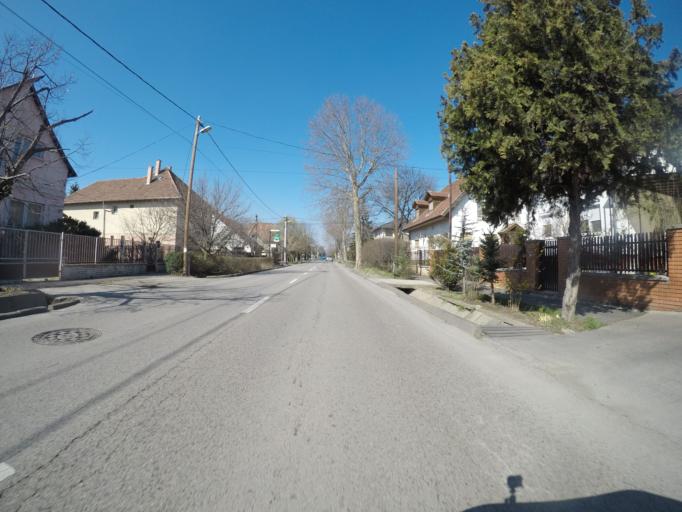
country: HU
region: Budapest
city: Budapest XVIII. keruelet
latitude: 47.4334
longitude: 19.1632
